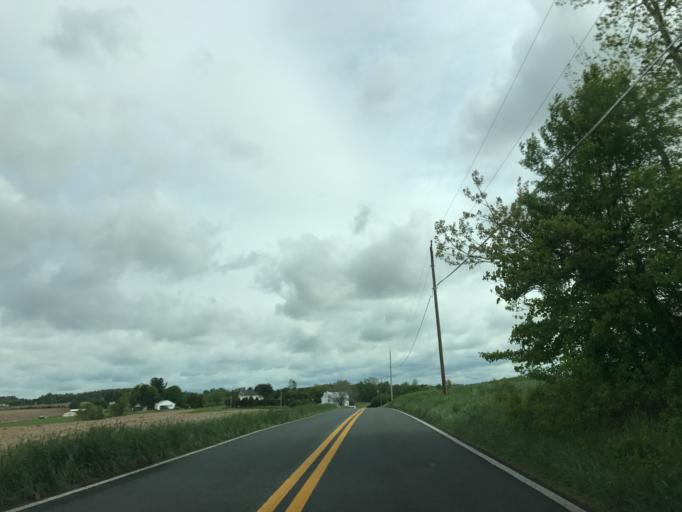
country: US
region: Maryland
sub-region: Carroll County
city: Hampstead
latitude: 39.5426
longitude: -76.8784
